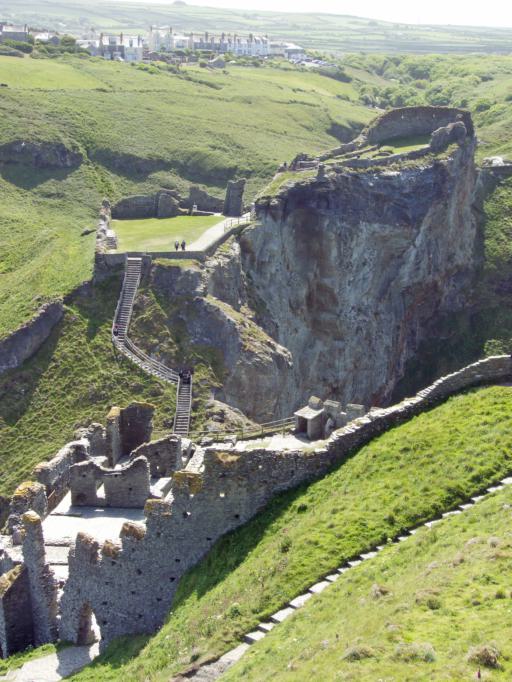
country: GB
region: England
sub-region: Cornwall
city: Tintagel
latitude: 50.6691
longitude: -4.7608
